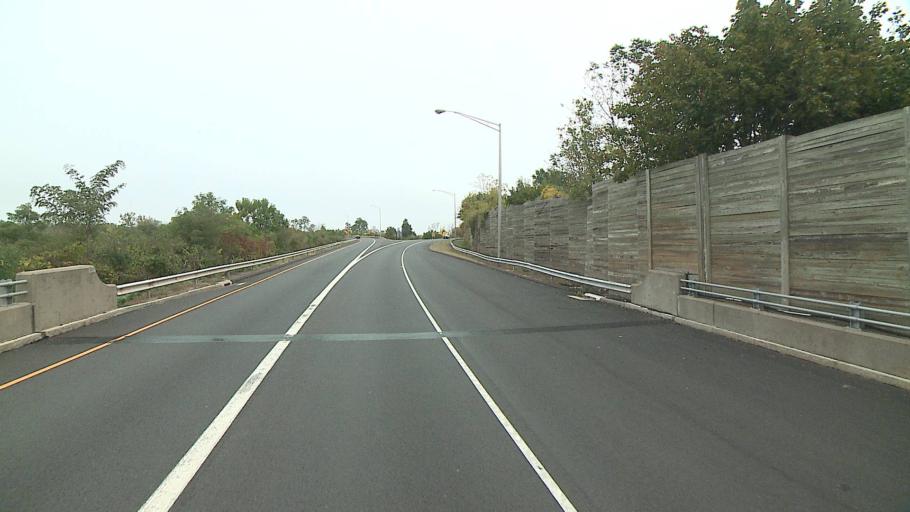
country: US
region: Connecticut
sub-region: Hartford County
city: West Hartford
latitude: 41.7233
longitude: -72.7707
